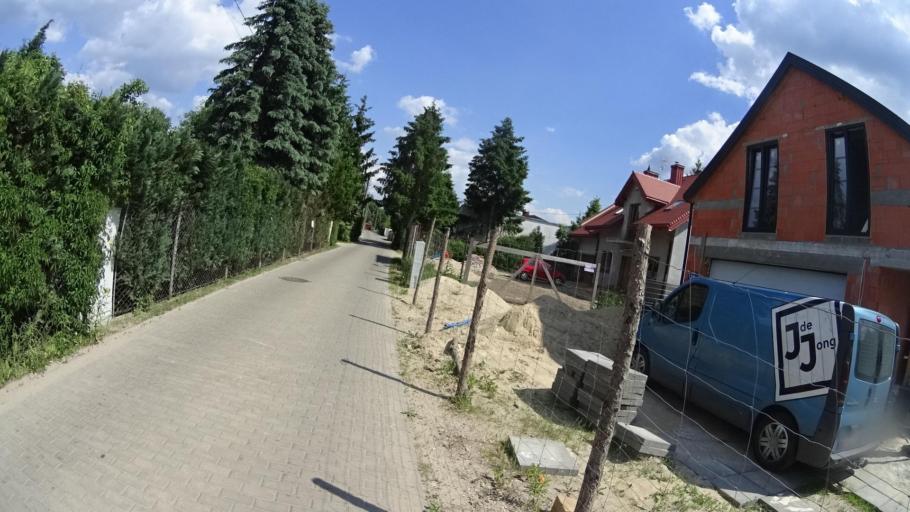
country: PL
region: Masovian Voivodeship
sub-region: Powiat piaseczynski
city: Konstancin-Jeziorna
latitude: 52.0927
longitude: 21.1093
